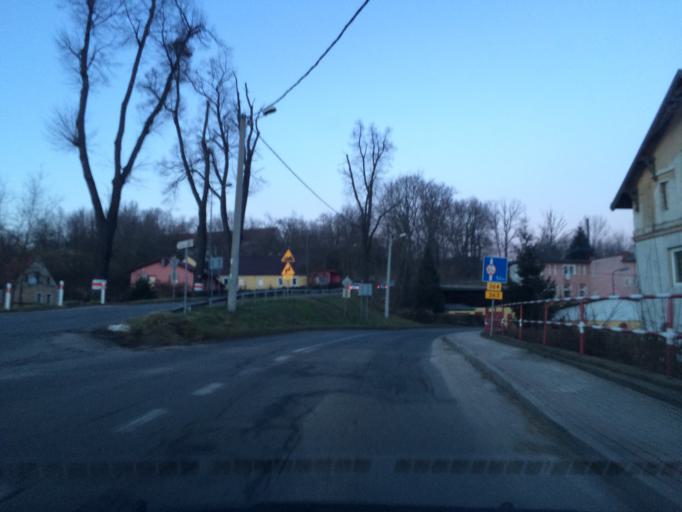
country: PL
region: Lower Silesian Voivodeship
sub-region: Powiat zlotoryjski
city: Zlotoryja
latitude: 51.1291
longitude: 15.9109
